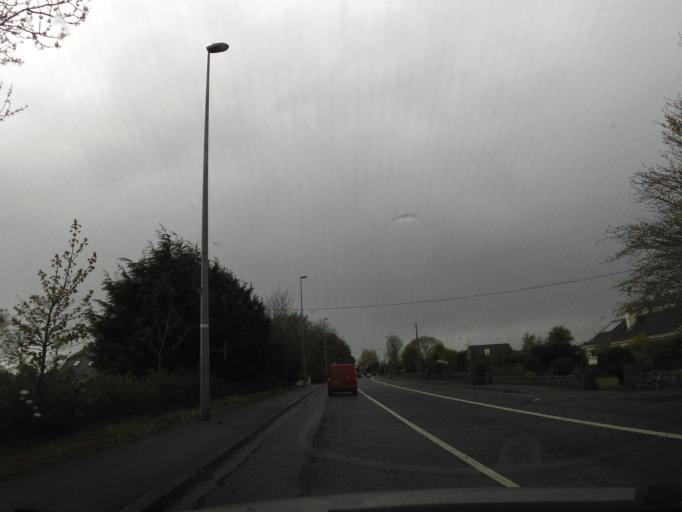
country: IE
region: Connaught
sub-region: County Galway
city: Claregalway
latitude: 53.3336
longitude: -8.9569
